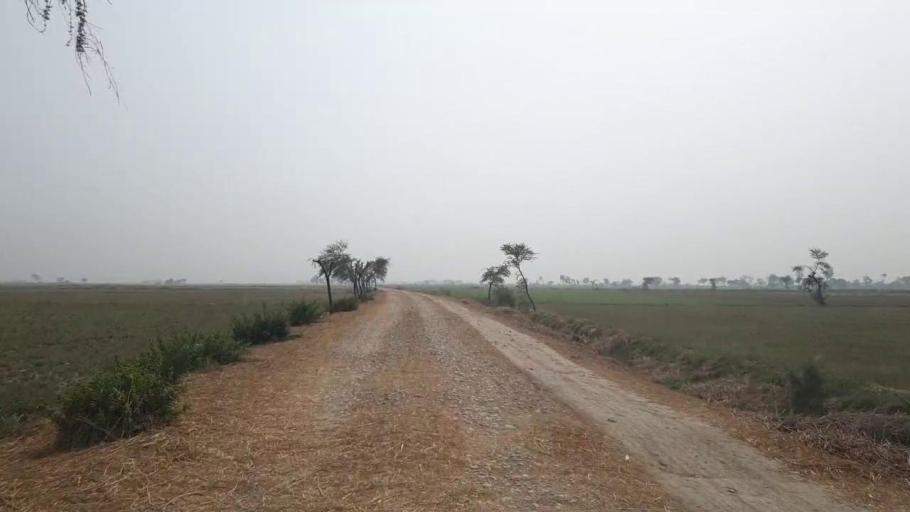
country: PK
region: Sindh
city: Kario
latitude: 24.6398
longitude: 68.5958
